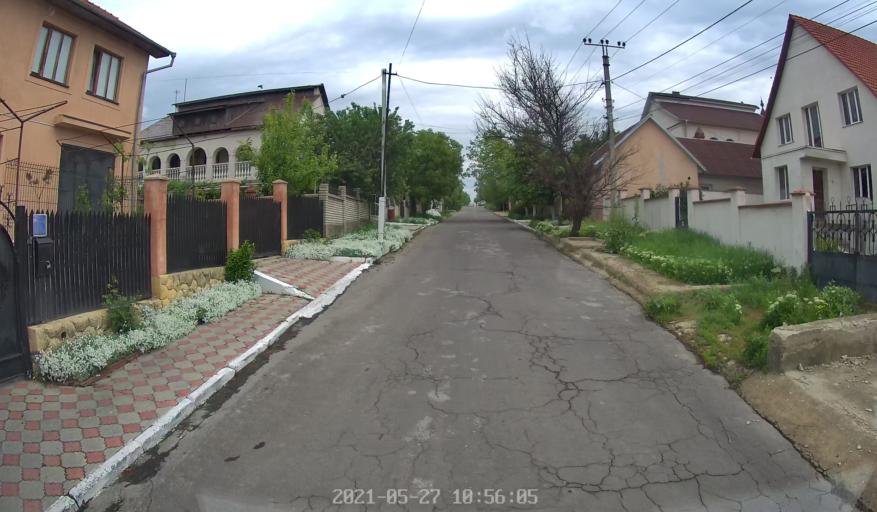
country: MD
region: Chisinau
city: Stauceni
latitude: 47.0971
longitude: 28.8663
